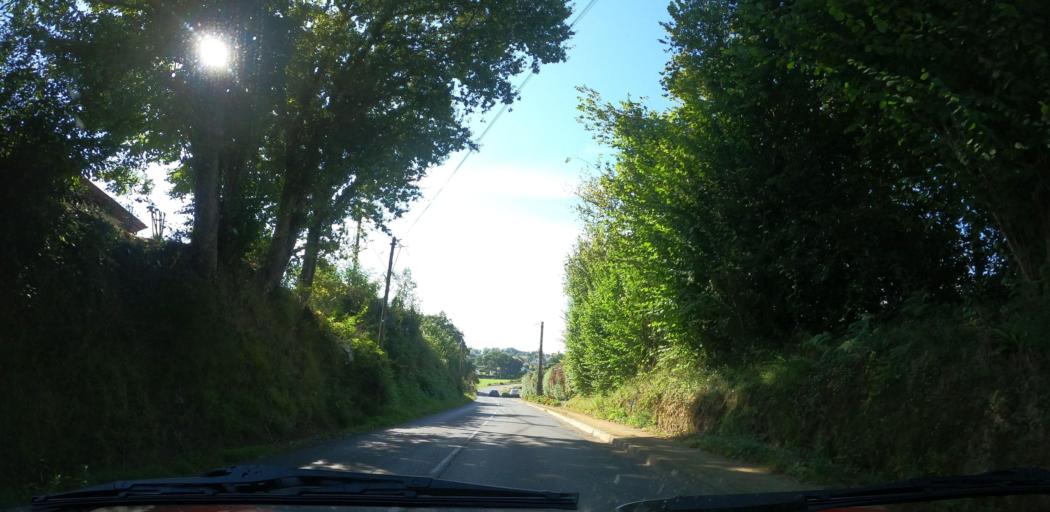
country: FR
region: Aquitaine
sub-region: Departement des Pyrenees-Atlantiques
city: Arbonne
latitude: 43.4158
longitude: -1.5486
